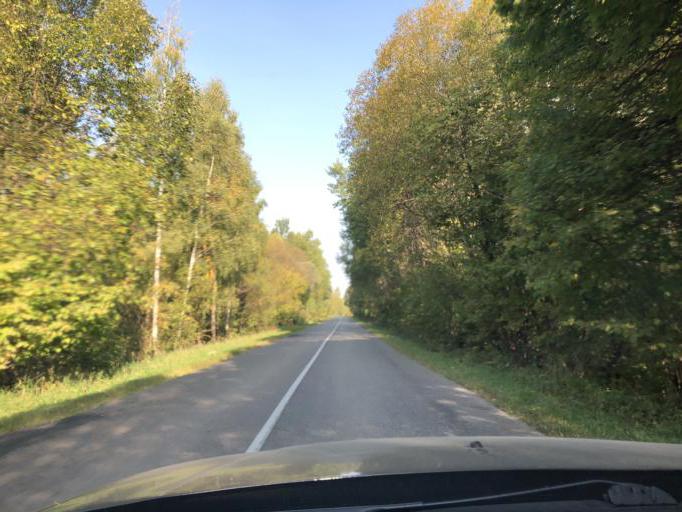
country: RU
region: Tula
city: Novogurovskiy
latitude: 54.3680
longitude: 37.3323
